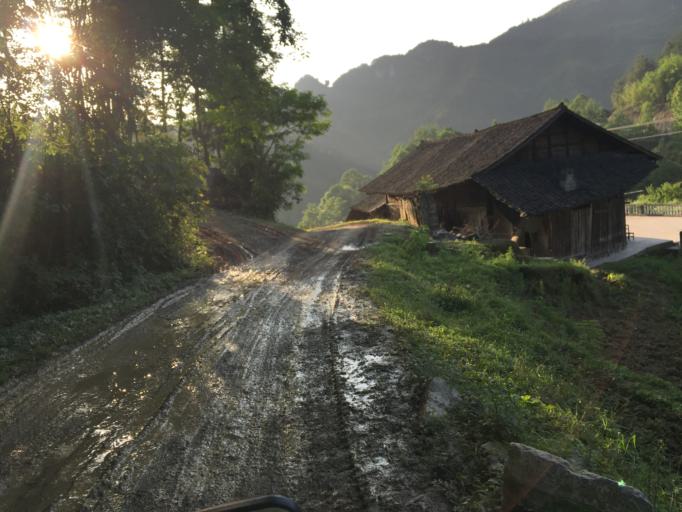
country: CN
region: Guizhou Sheng
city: Xujiaba
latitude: 27.7315
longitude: 108.0204
